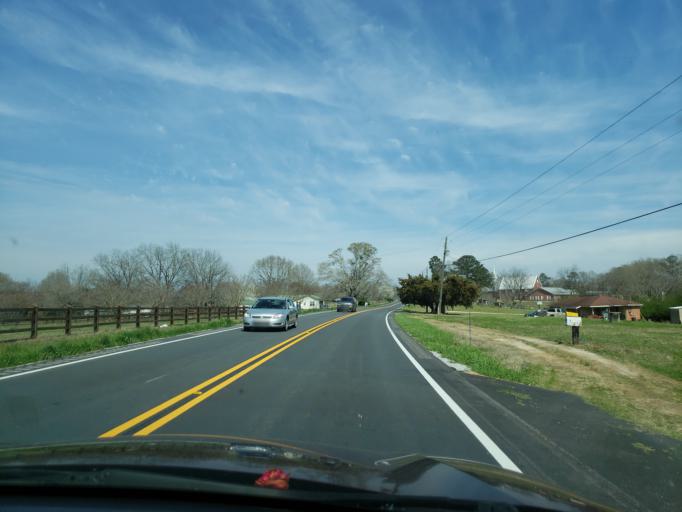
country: US
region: Alabama
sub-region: Elmore County
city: Tallassee
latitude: 32.5780
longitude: -85.7584
